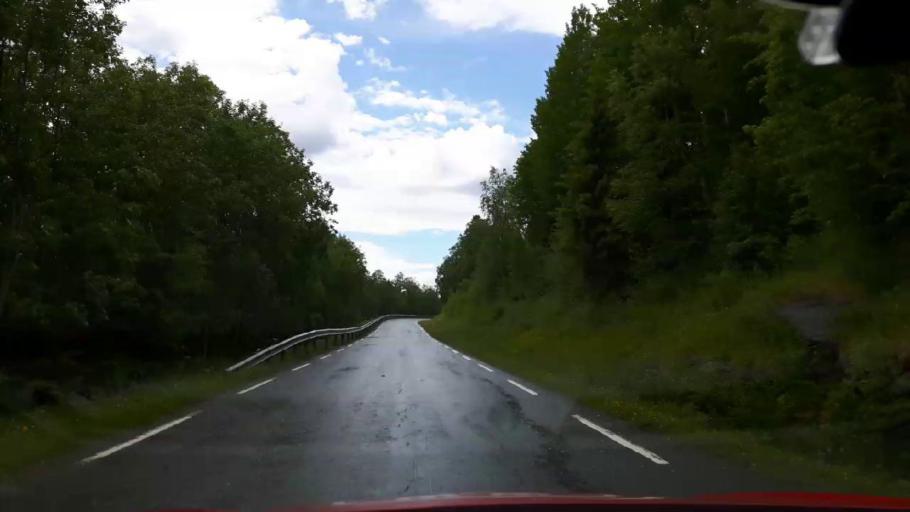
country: NO
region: Nord-Trondelag
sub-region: Lierne
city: Sandvika
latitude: 64.1059
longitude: 13.9897
